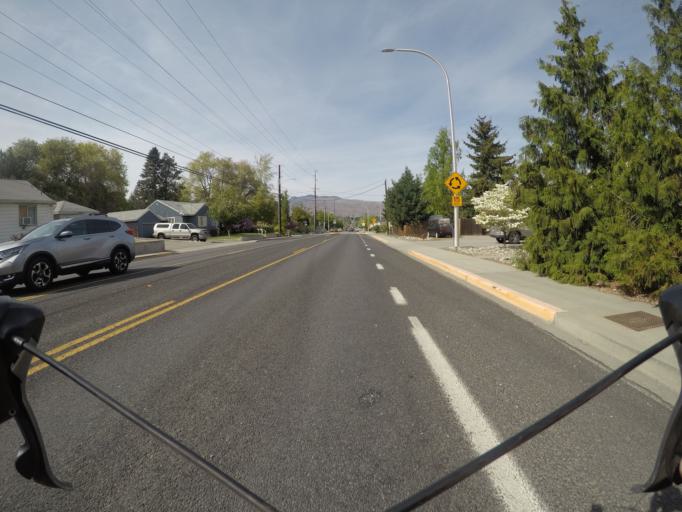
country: US
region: Washington
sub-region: Chelan County
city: West Wenatchee
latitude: 47.4363
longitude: -120.3463
